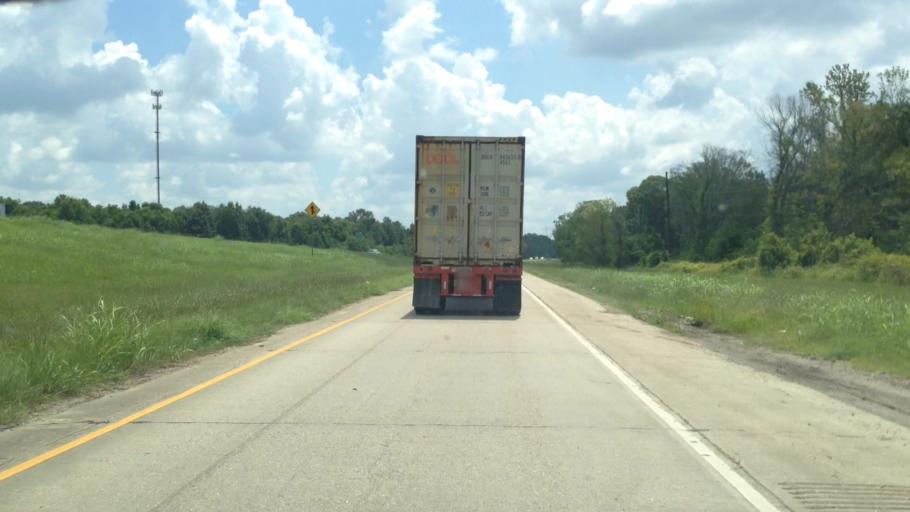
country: US
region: Louisiana
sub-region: Ascension Parish
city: Sorrento
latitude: 30.1704
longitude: -90.8749
